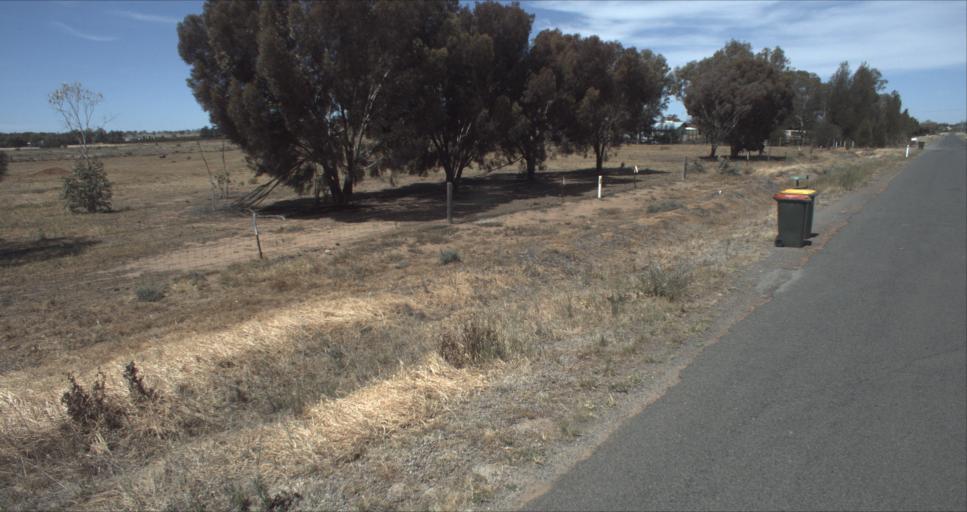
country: AU
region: New South Wales
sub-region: Leeton
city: Leeton
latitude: -34.5993
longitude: 146.4273
